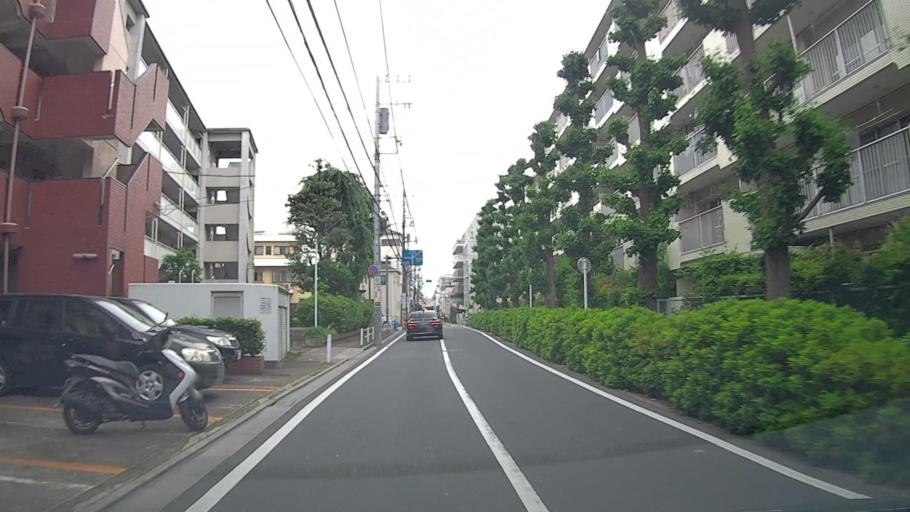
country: JP
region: Saitama
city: Shimotoda
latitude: 35.7646
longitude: 139.6812
